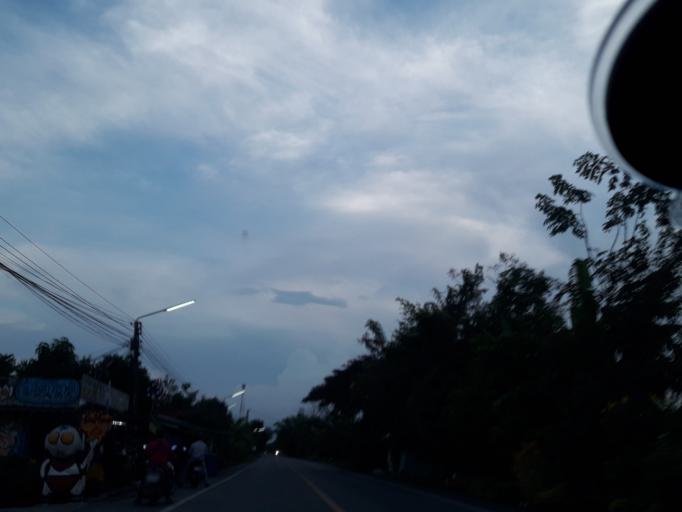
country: TH
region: Pathum Thani
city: Nong Suea
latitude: 14.1224
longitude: 100.8690
